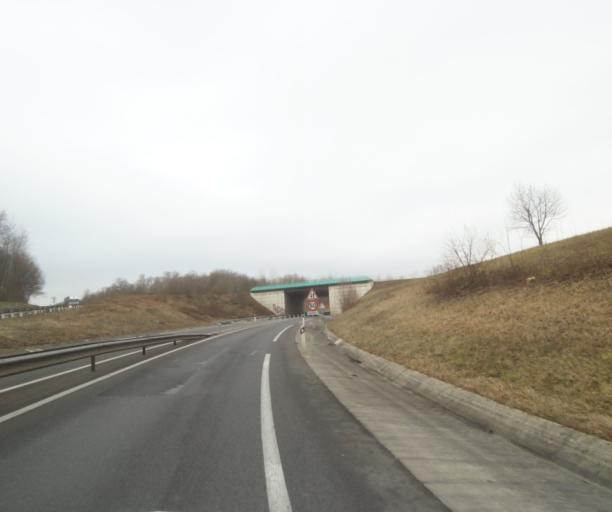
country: FR
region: Champagne-Ardenne
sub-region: Departement de la Haute-Marne
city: Bettancourt-la-Ferree
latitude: 48.6200
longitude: 4.9846
